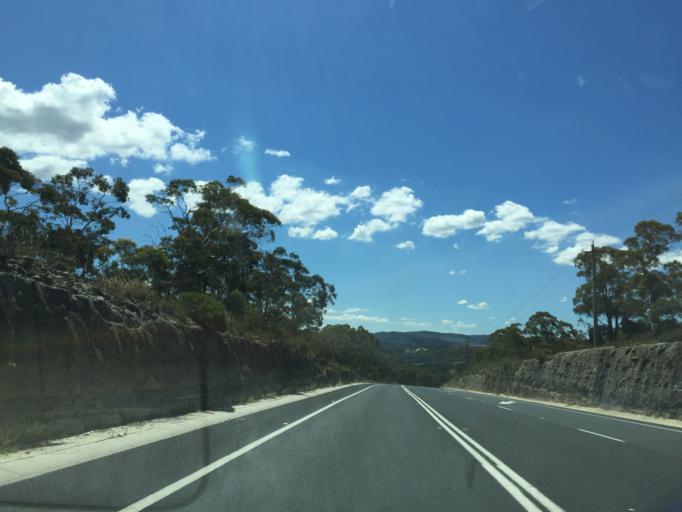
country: AU
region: New South Wales
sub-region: Lithgow
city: Lithgow
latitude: -33.4164
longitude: 150.1004
